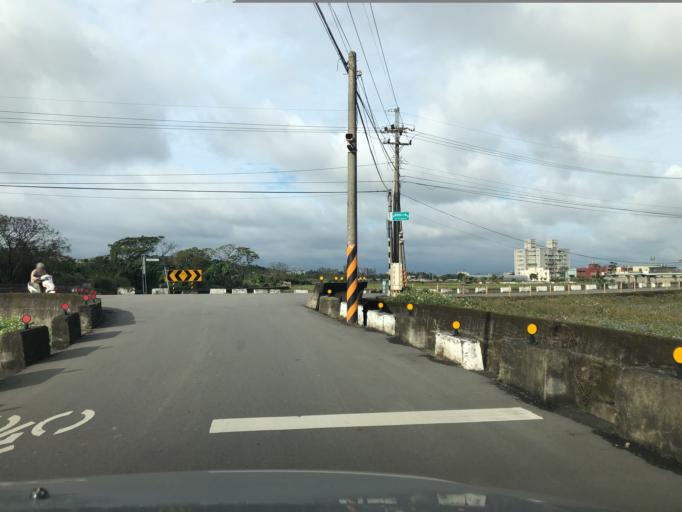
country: TW
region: Taiwan
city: Daxi
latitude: 24.9188
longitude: 121.2594
